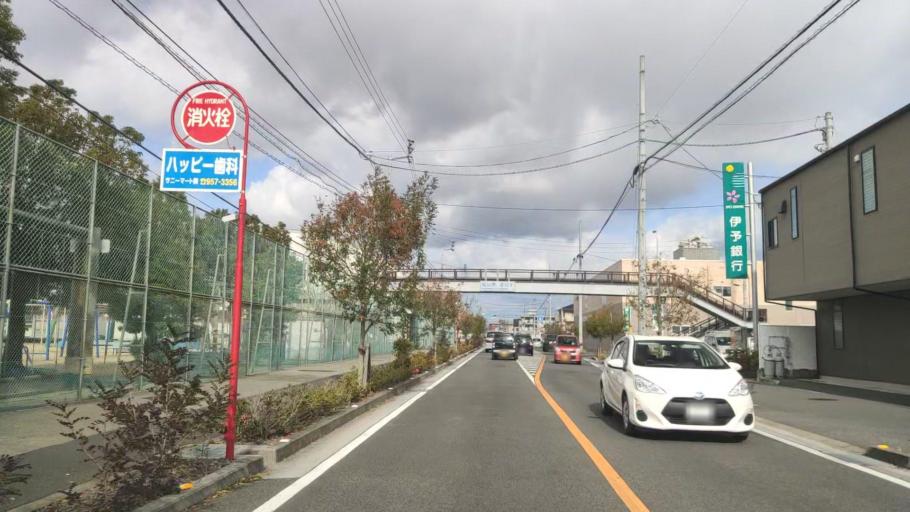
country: JP
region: Ehime
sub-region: Shikoku-chuo Shi
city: Matsuyama
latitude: 33.8106
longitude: 132.7608
